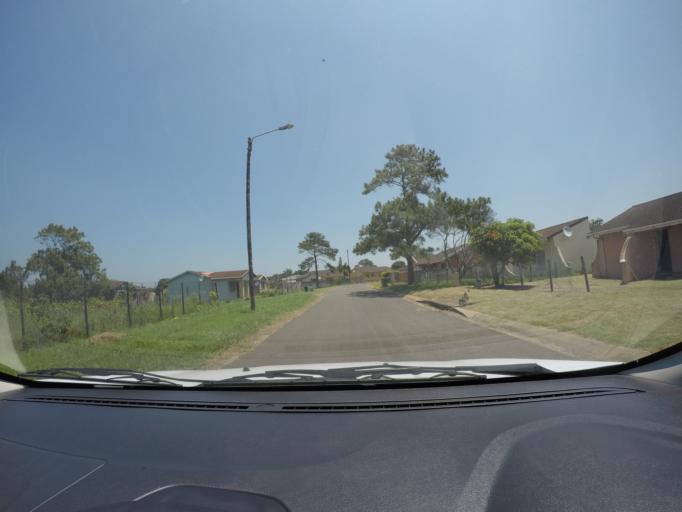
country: ZA
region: KwaZulu-Natal
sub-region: uThungulu District Municipality
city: eSikhawini
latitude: -28.8901
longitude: 31.8847
